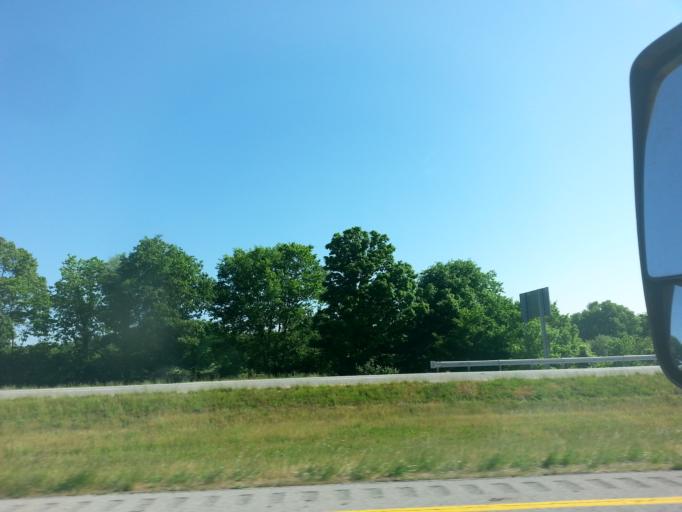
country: US
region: Kentucky
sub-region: Shelby County
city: Shelbyville
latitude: 38.1868
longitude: -85.2527
